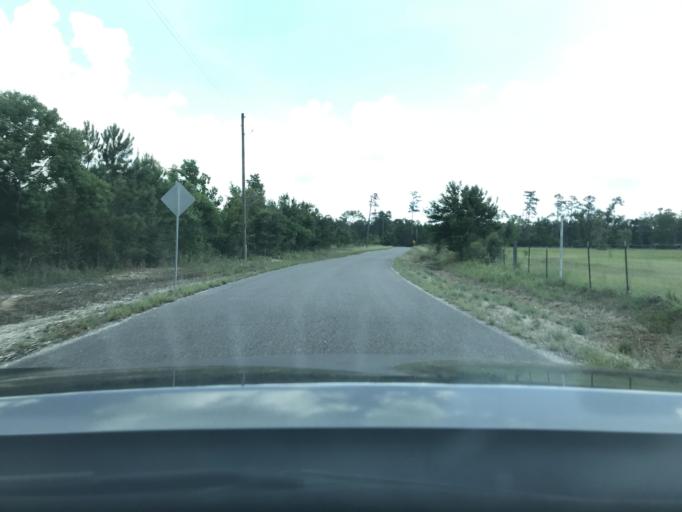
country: US
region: Louisiana
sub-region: Calcasieu Parish
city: Moss Bluff
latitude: 30.3381
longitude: -93.1281
